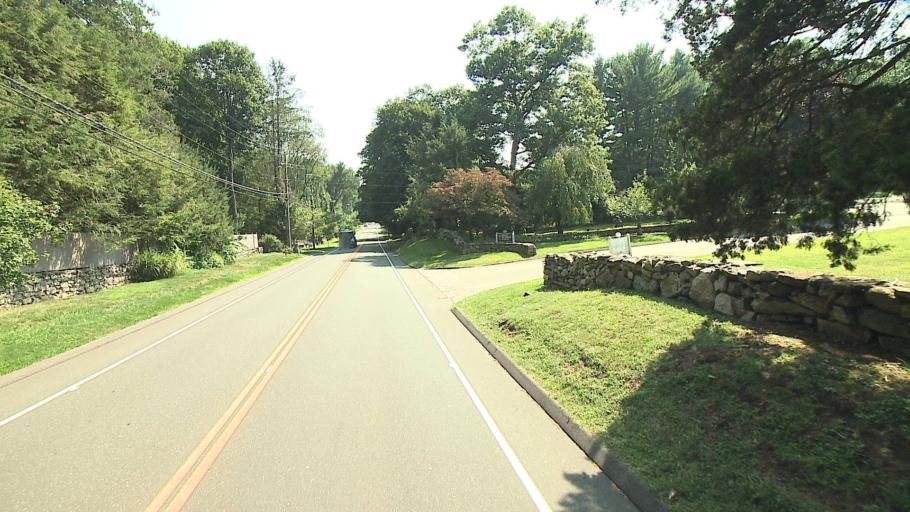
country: US
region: Connecticut
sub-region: Fairfield County
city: Westport
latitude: 41.1685
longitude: -73.3613
